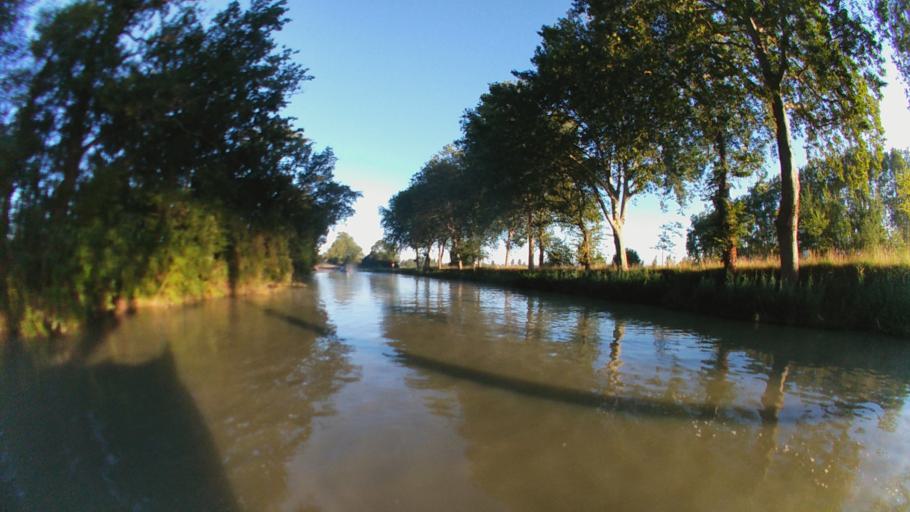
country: FR
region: Midi-Pyrenees
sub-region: Departement de la Haute-Garonne
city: Villenouvelle
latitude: 43.4119
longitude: 1.6600
